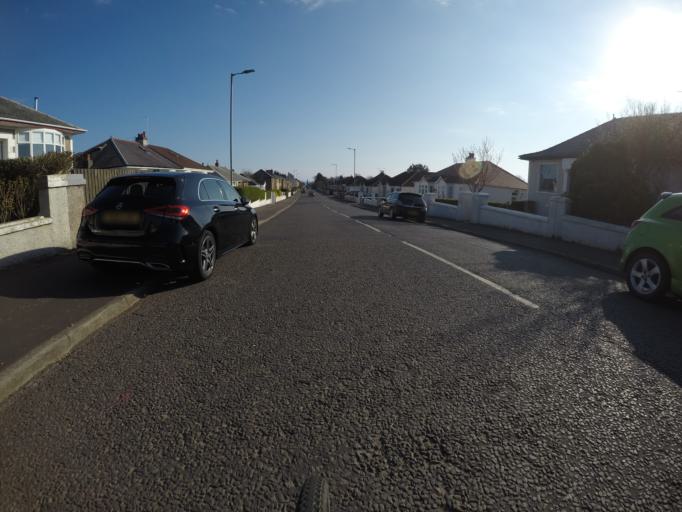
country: GB
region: Scotland
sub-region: North Ayrshire
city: Saltcoats
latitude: 55.6415
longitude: -4.7810
